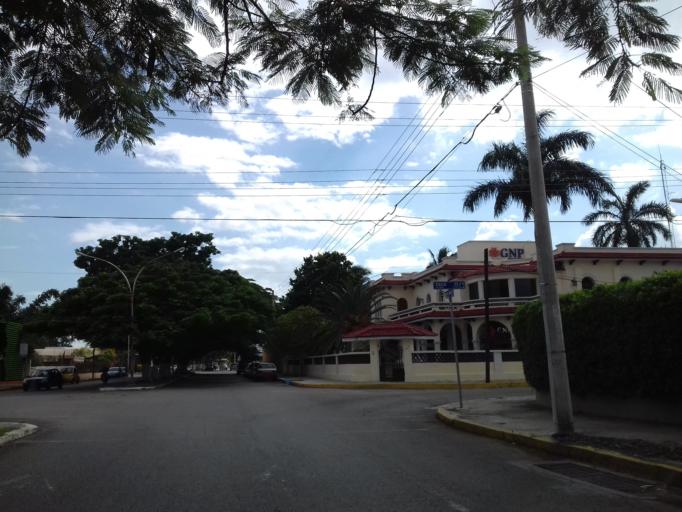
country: MX
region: Yucatan
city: Merida
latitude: 21.0008
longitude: -89.6110
